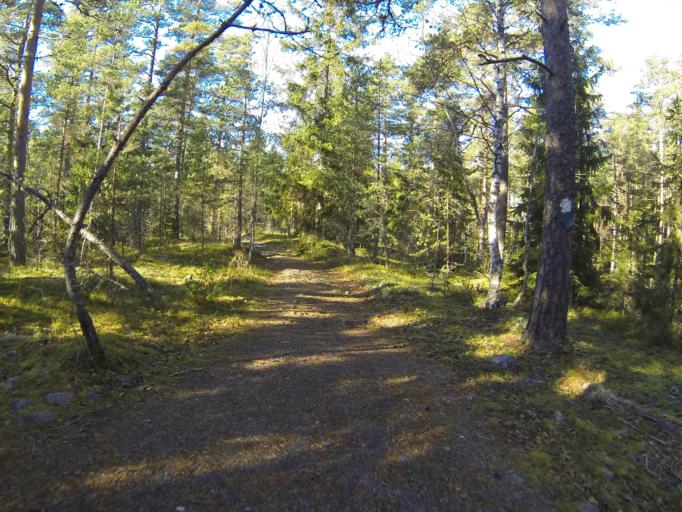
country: FI
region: Varsinais-Suomi
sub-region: Salo
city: Saerkisalo
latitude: 60.1981
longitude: 22.9284
